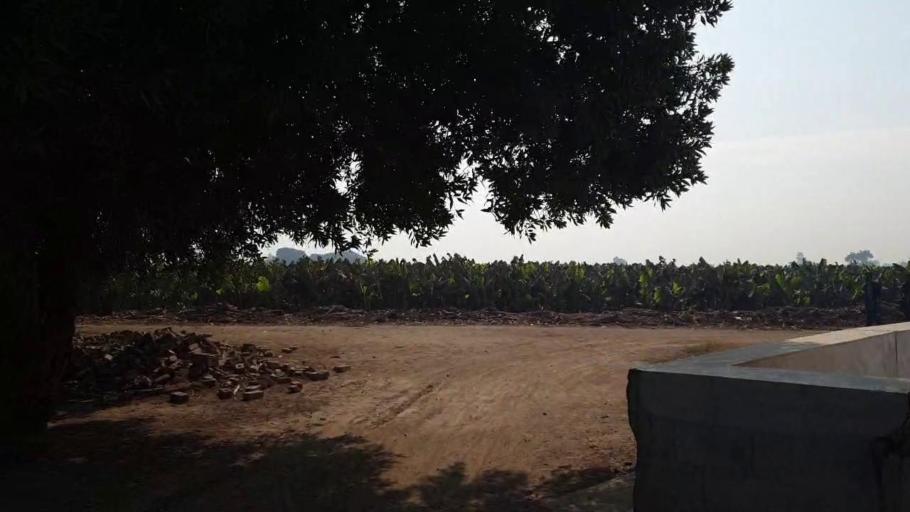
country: PK
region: Sindh
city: Chambar
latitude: 25.3804
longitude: 68.7744
